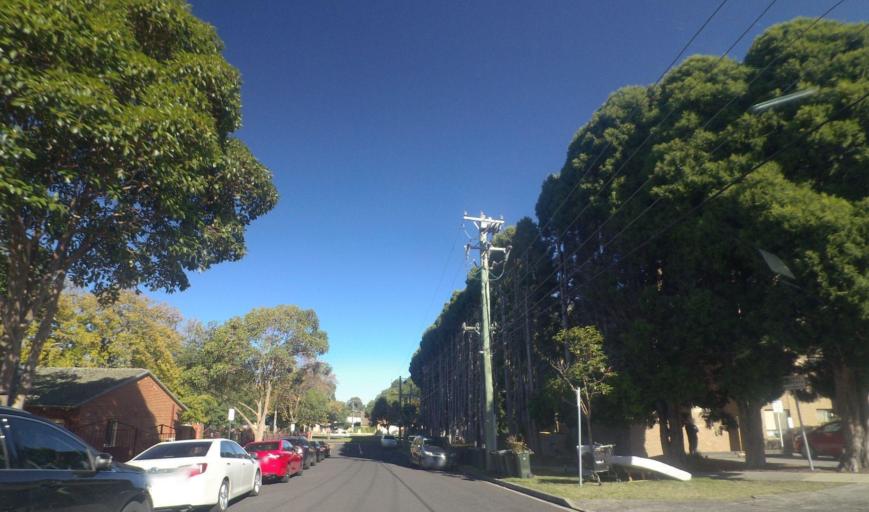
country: AU
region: Victoria
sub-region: Whitehorse
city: Box Hill
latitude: -37.8179
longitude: 145.1291
